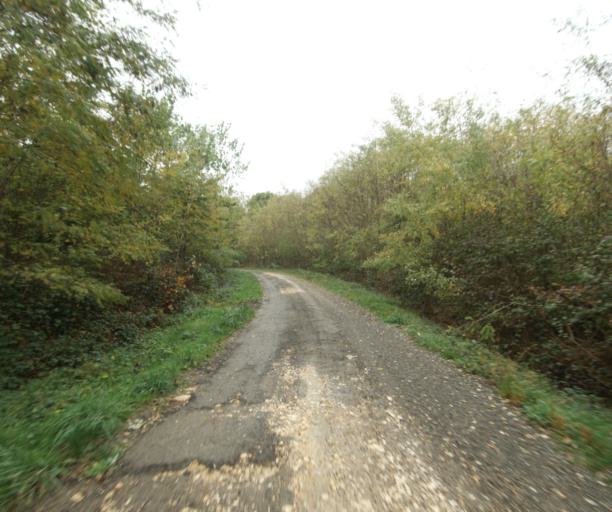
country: FR
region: Bourgogne
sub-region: Departement de Saone-et-Loire
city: Tournus
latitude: 46.4872
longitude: 4.8489
